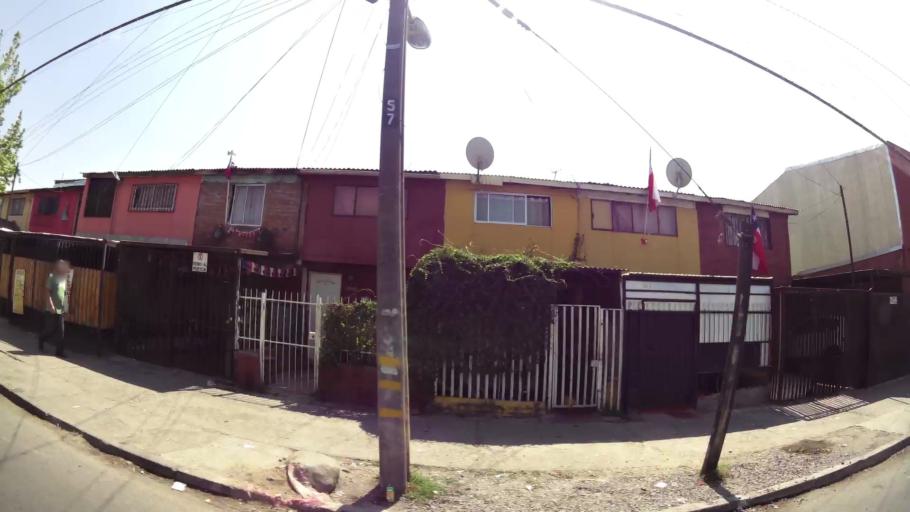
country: CL
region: Santiago Metropolitan
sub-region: Provincia de Santiago
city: La Pintana
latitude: -33.5557
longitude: -70.6128
